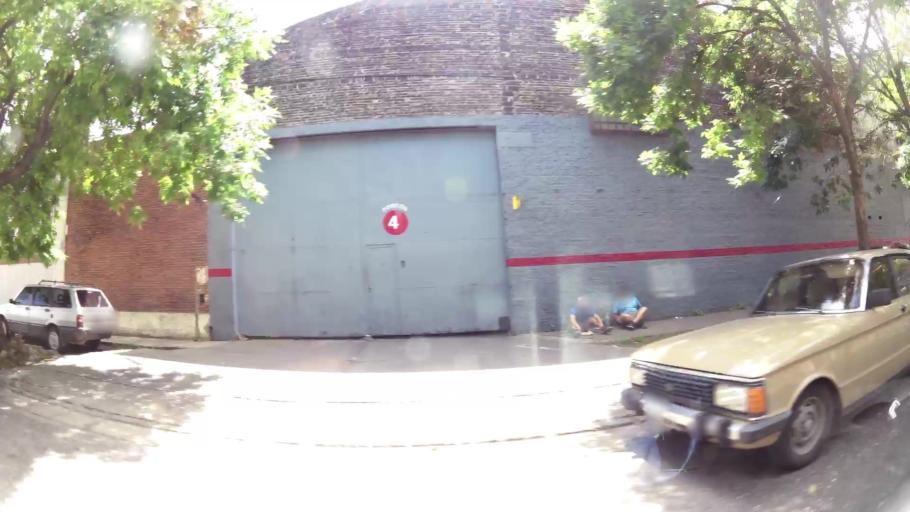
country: AR
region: Santa Fe
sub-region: Departamento de Rosario
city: Rosario
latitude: -32.9711
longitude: -60.6308
